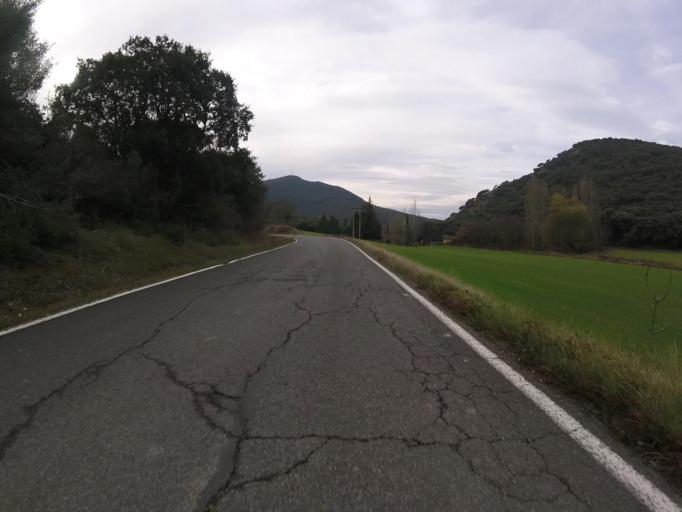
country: ES
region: Navarre
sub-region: Provincia de Navarra
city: Estella
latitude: 42.7029
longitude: -2.0532
